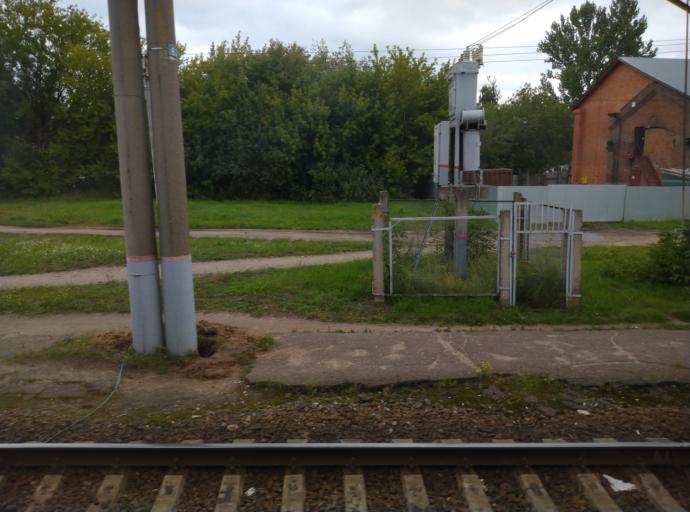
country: RU
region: Kostroma
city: Nerekhta
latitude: 57.4628
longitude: 40.5509
